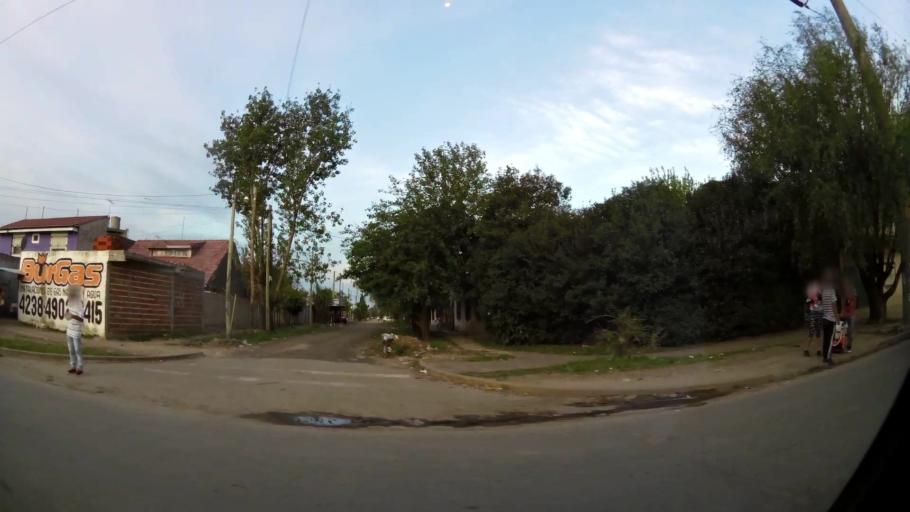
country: AR
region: Buenos Aires
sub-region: Partido de Almirante Brown
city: Adrogue
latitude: -34.7974
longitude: -58.3069
